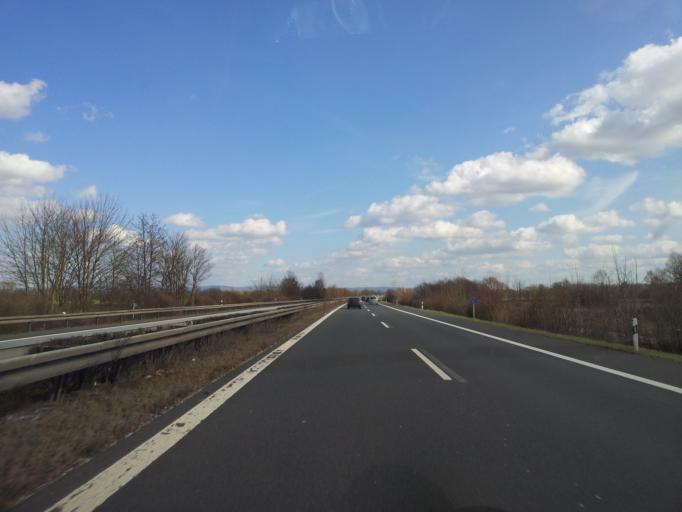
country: DE
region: Bavaria
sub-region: Upper Franconia
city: Oberhaid
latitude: 49.9236
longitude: 10.8222
